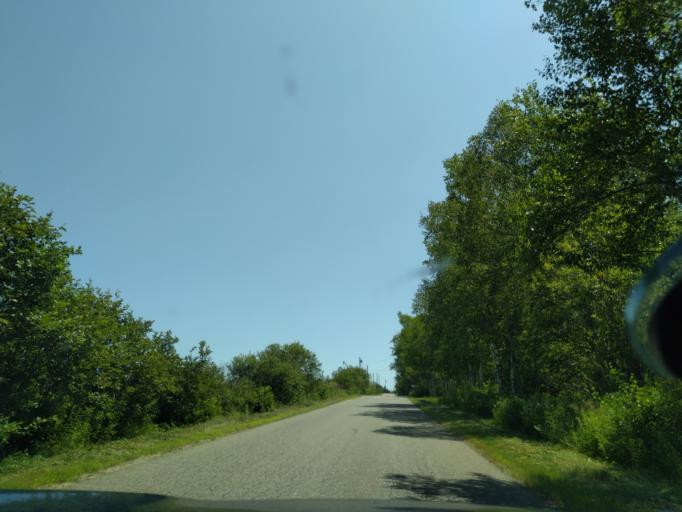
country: US
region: Maine
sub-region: Washington County
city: Eastport
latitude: 44.8320
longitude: -67.0071
